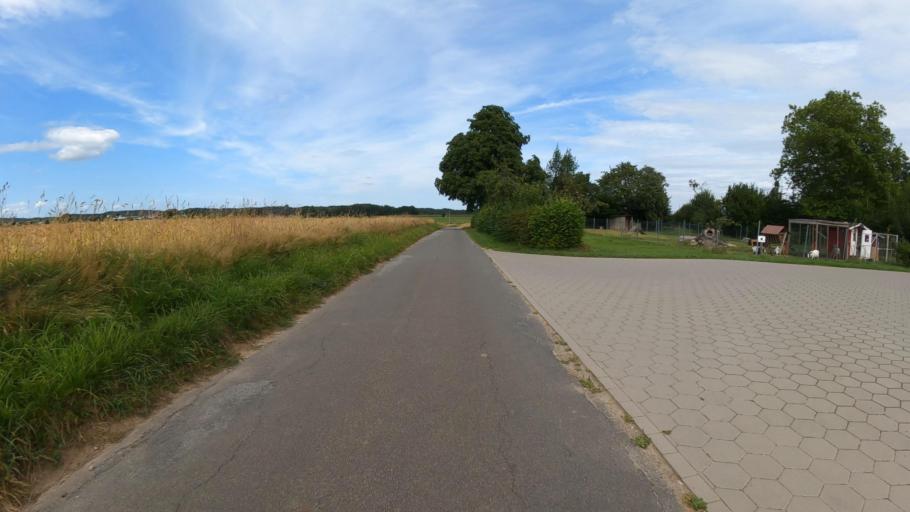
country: DE
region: Lower Saxony
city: Seevetal
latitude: 53.4115
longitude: 9.9699
